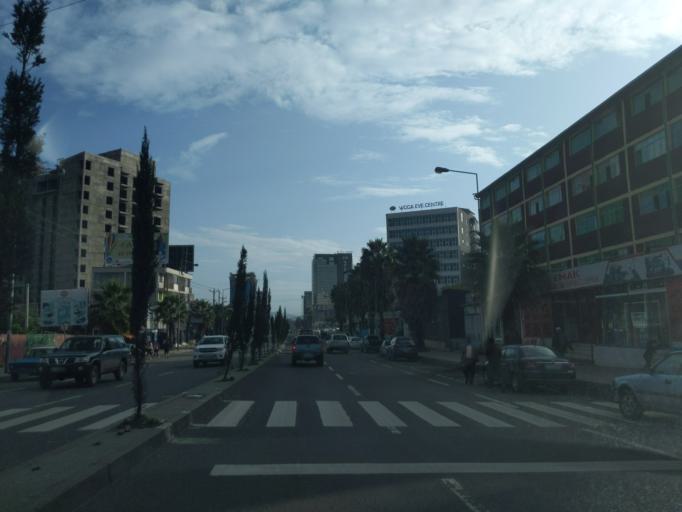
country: ET
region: Adis Abeba
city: Addis Ababa
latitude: 8.9849
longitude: 38.7671
